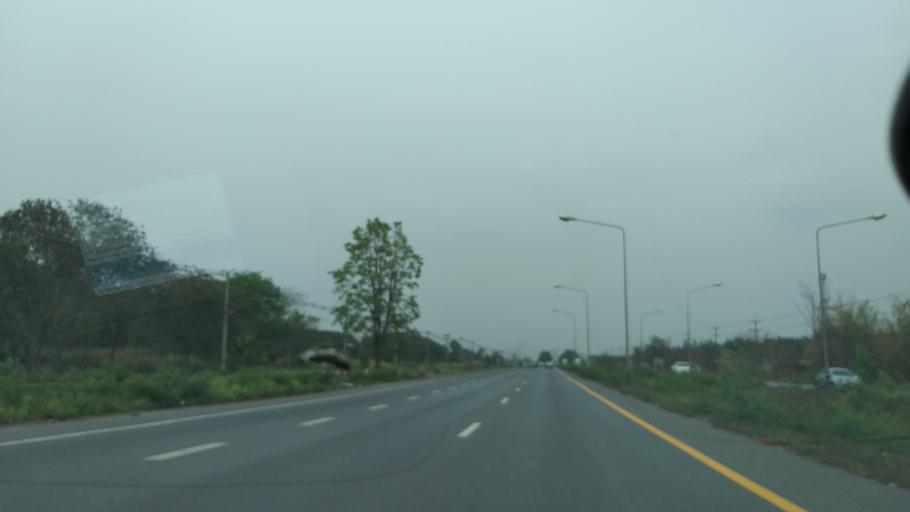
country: TH
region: Chon Buri
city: Ko Chan
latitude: 13.2905
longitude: 101.2585
